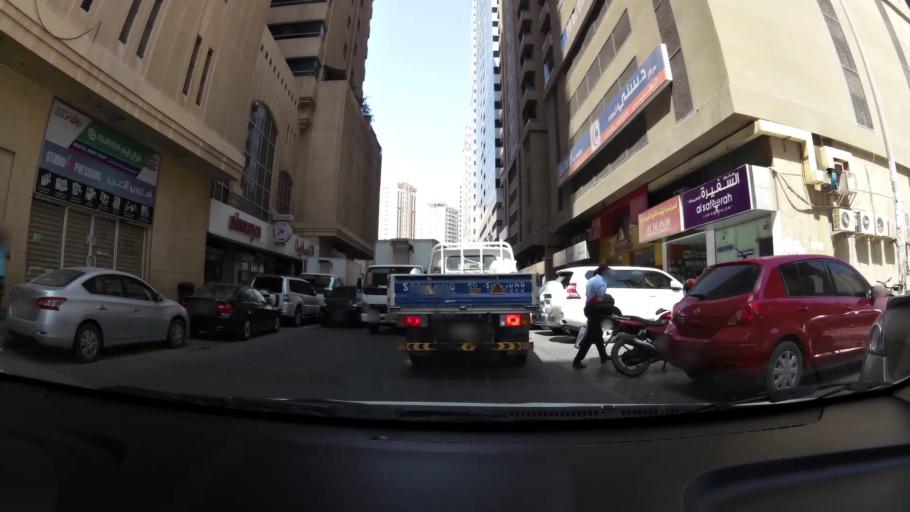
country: AE
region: Ash Shariqah
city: Sharjah
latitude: 25.3007
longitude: 55.3735
